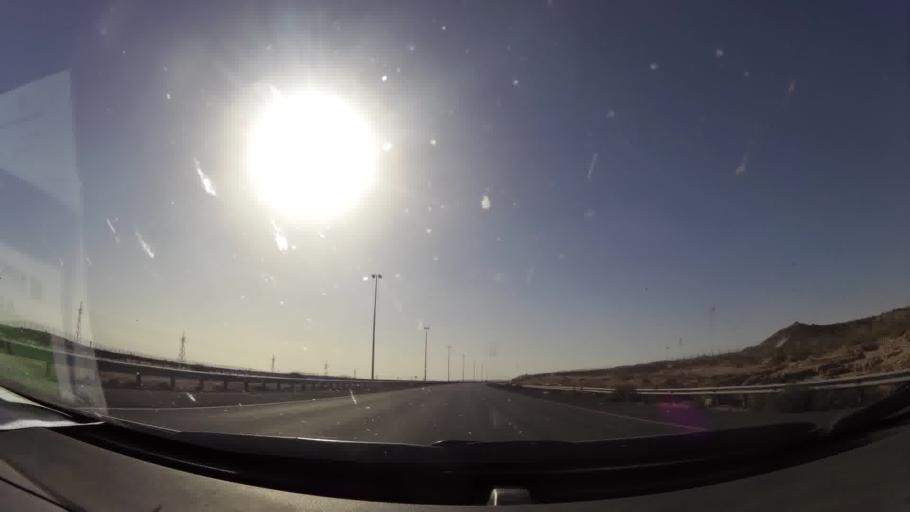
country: KW
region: Al Asimah
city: Kuwait City
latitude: 29.5486
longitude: 47.8713
